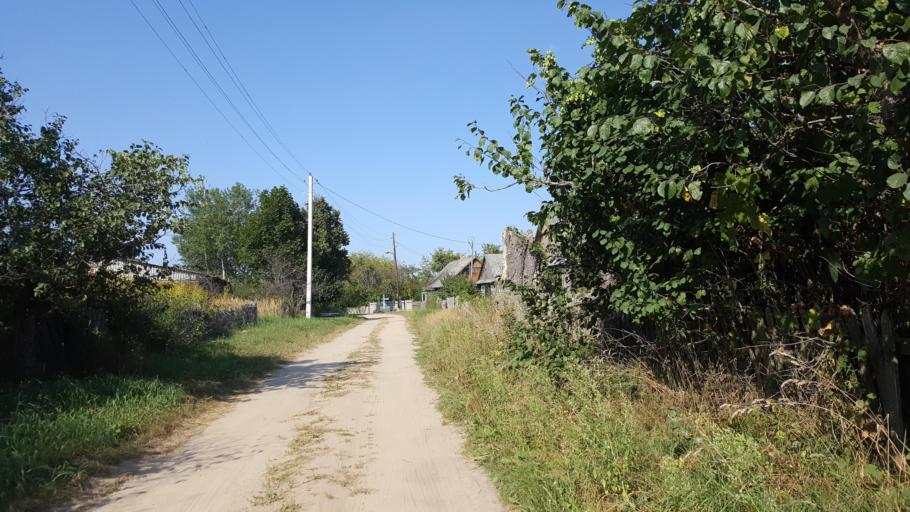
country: BY
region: Brest
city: Kamyanyuki
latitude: 52.5698
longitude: 23.6284
